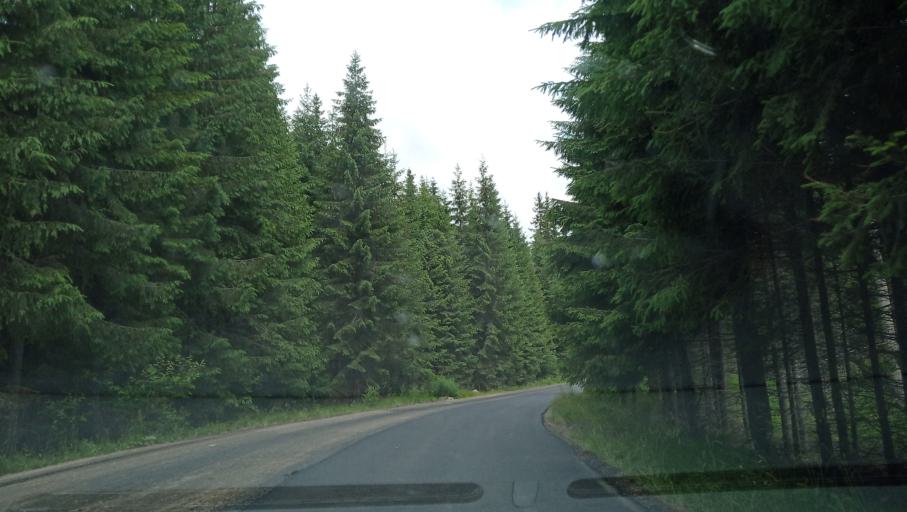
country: RO
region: Gorj
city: Novaci-Straini
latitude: 45.4204
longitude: 23.6974
